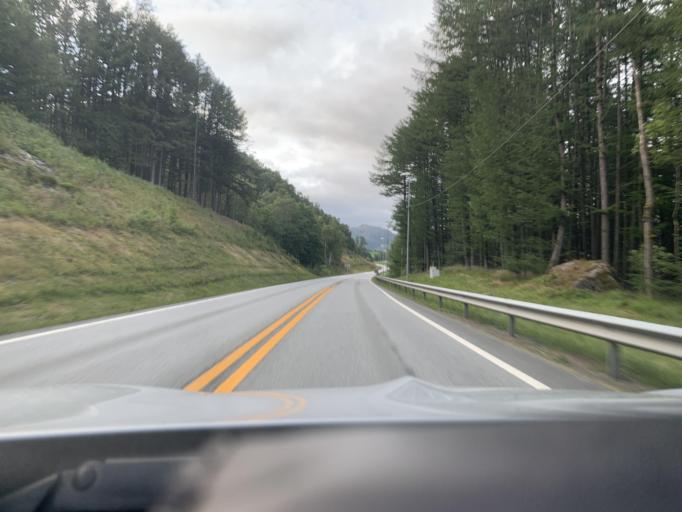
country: NO
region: Rogaland
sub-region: Bjerkreim
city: Vikesa
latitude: 58.5963
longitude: 6.0798
